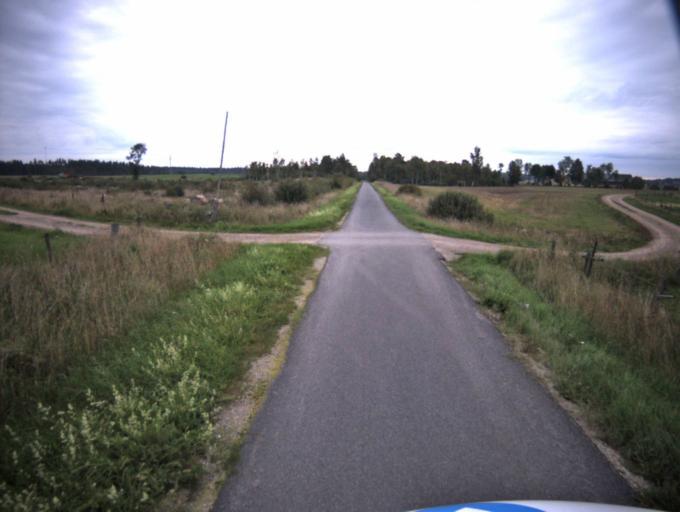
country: SE
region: Vaestra Goetaland
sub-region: Falkopings Kommun
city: Falkoeping
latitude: 57.9933
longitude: 13.5400
